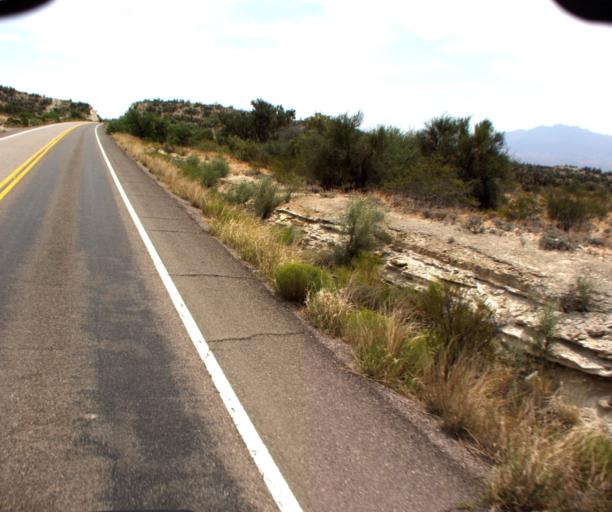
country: US
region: Arizona
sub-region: Gila County
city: Peridot
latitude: 33.2630
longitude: -110.3011
